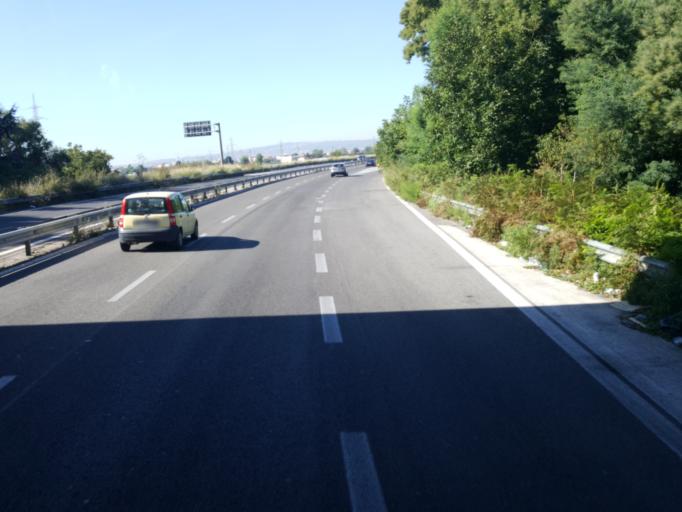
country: IT
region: Campania
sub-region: Provincia di Napoli
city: Pascarola
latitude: 40.9687
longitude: 14.2921
